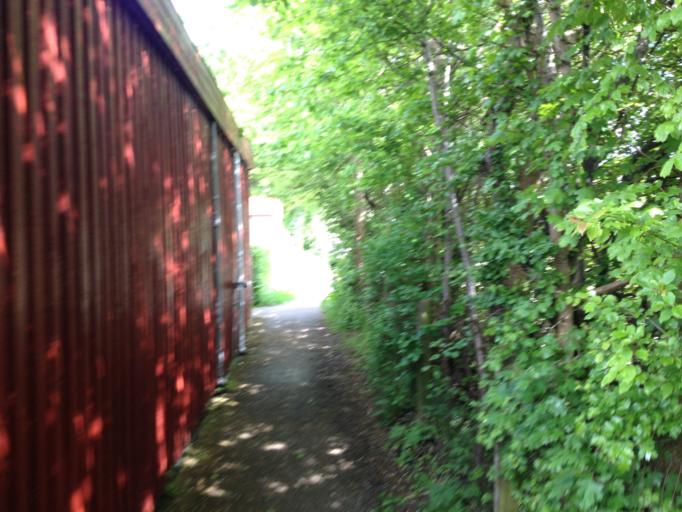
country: DK
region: Capital Region
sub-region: Fredensborg Kommune
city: Niva
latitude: 55.9384
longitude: 12.5246
